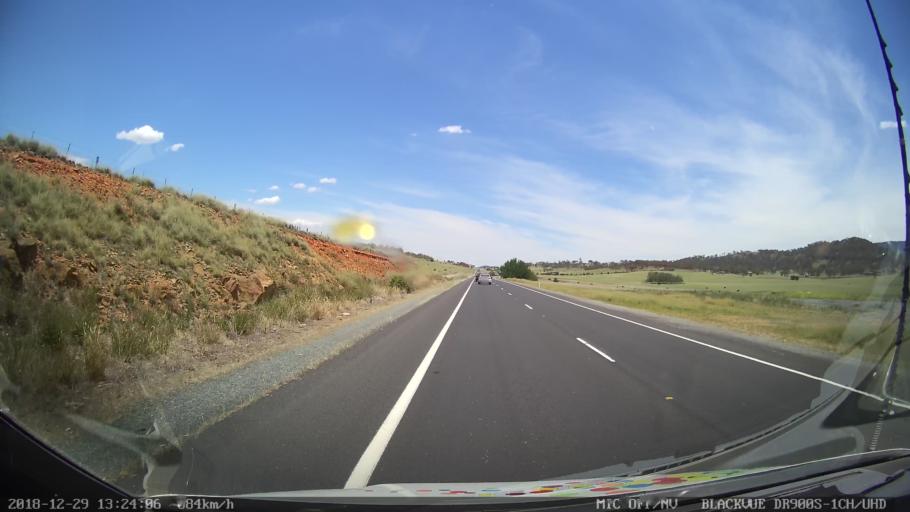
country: AU
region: New South Wales
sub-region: Cooma-Monaro
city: Cooma
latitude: -35.8252
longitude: 149.1628
